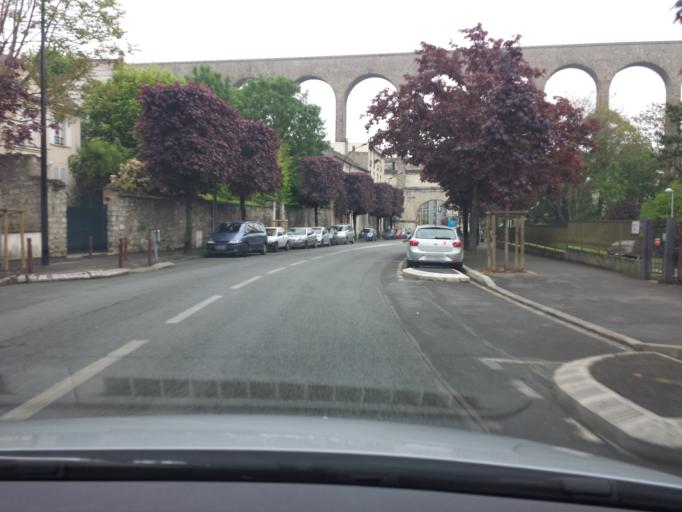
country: FR
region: Ile-de-France
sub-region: Departement du Val-de-Marne
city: Arcueil
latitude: 48.7985
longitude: 2.3310
